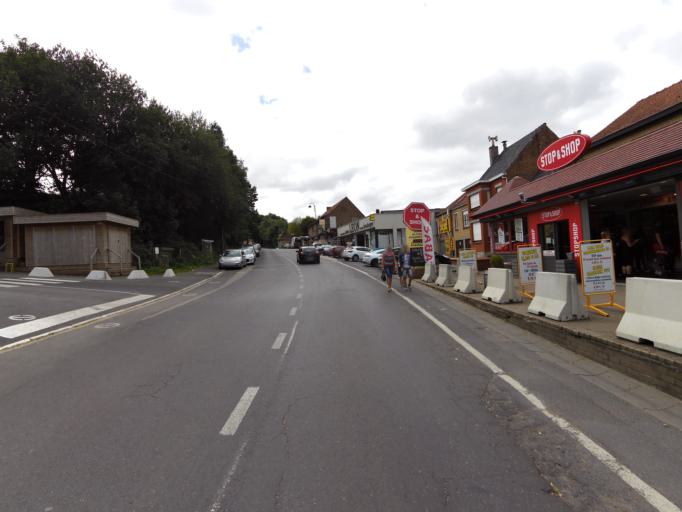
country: FR
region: Nord-Pas-de-Calais
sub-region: Departement du Nord
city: Saint-Jans-Cappel
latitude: 50.7811
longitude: 2.7394
